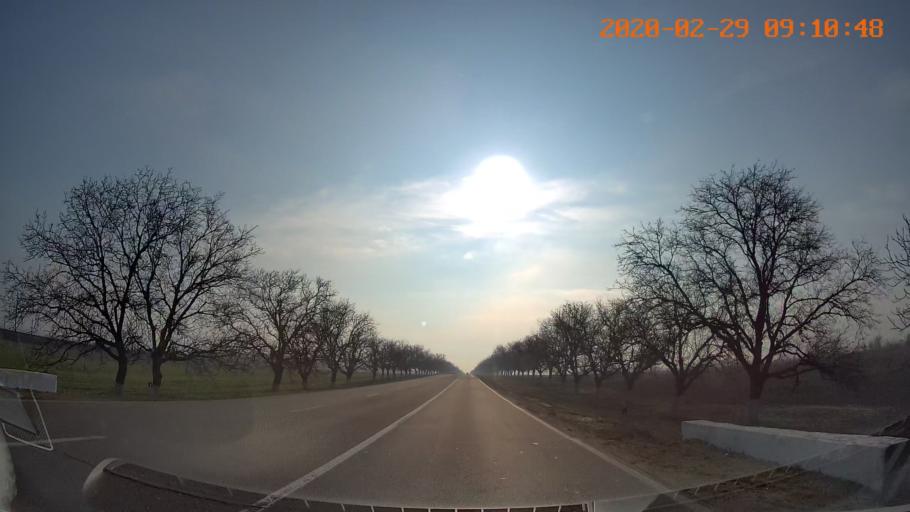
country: MD
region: Telenesti
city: Slobozia
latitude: 46.8408
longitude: 29.7886
